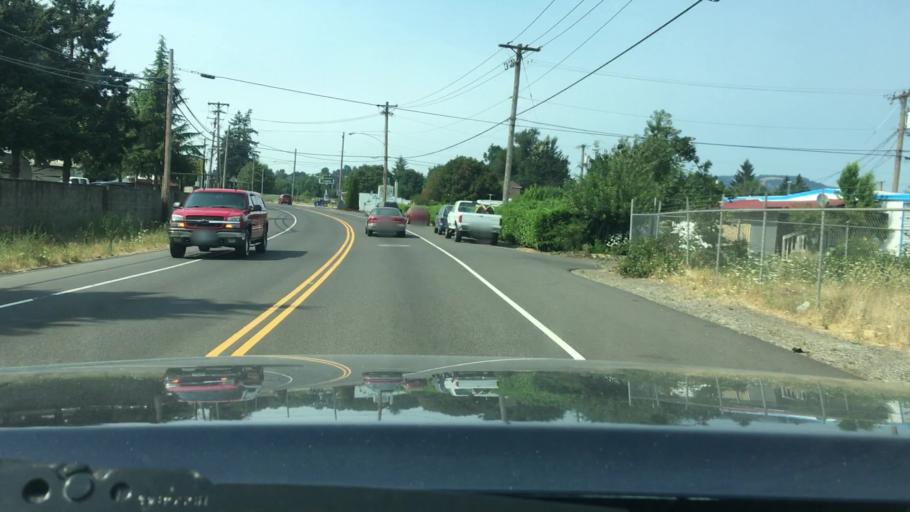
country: US
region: Oregon
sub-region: Lane County
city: Springfield
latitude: 44.0370
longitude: -123.0272
